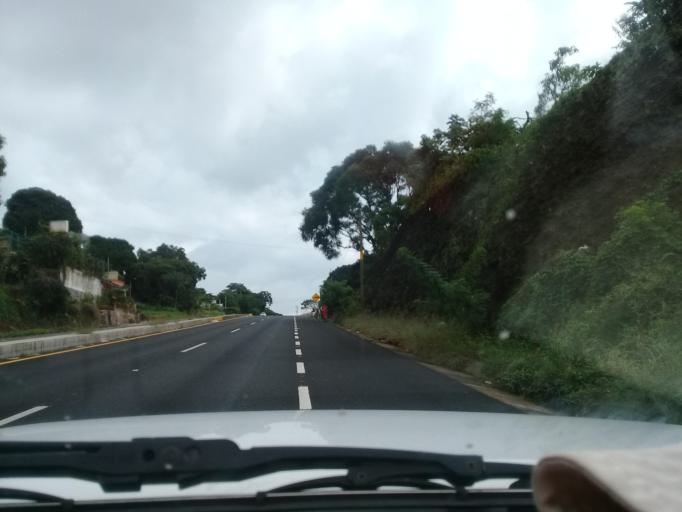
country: MX
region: Veracruz
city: Catemaco
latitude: 18.4292
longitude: -95.1264
